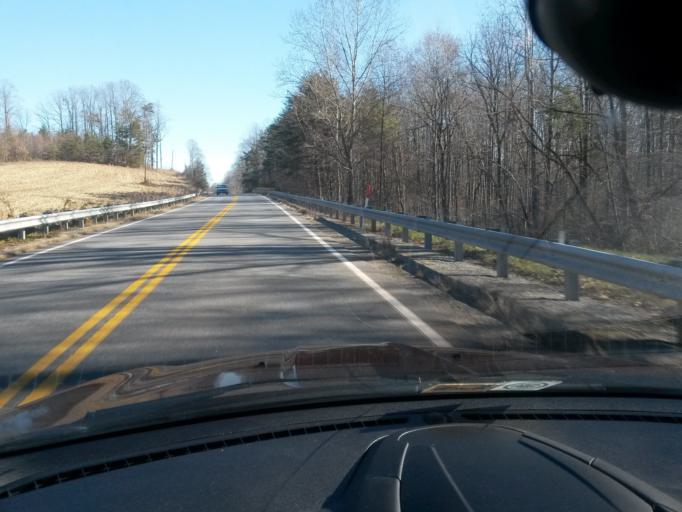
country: US
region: Virginia
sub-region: Patrick County
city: Patrick Springs
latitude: 36.7690
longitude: -80.1543
